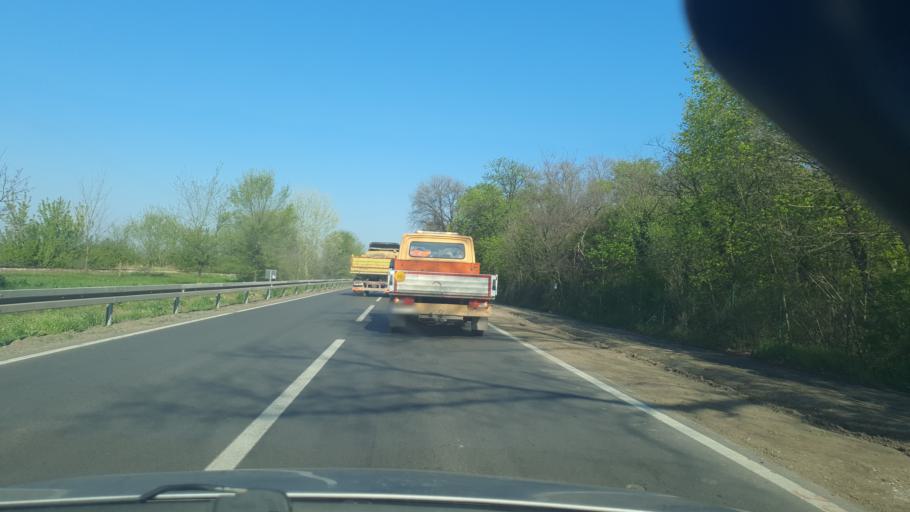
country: RS
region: Autonomna Pokrajina Vojvodina
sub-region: Juznobacki Okrug
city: Vrbas
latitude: 45.5898
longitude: 19.5957
